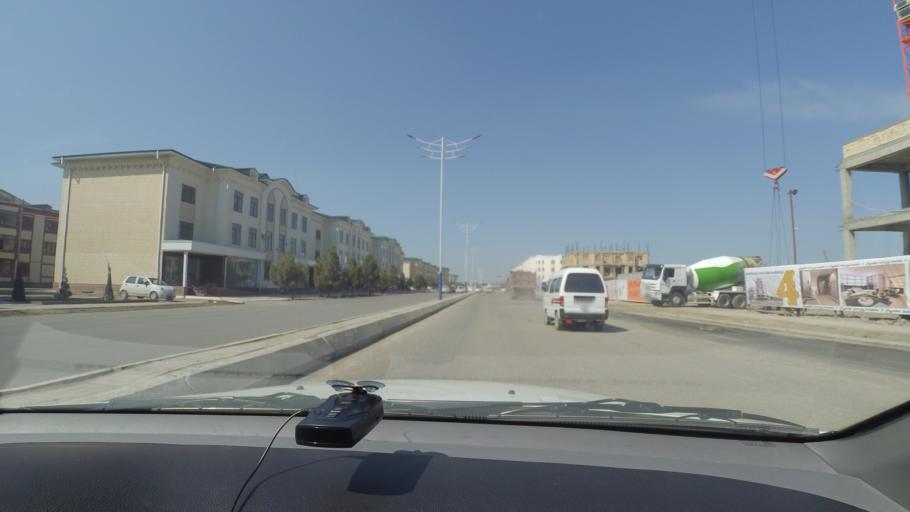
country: UZ
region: Bukhara
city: Bukhara
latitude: 39.7802
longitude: 64.4362
